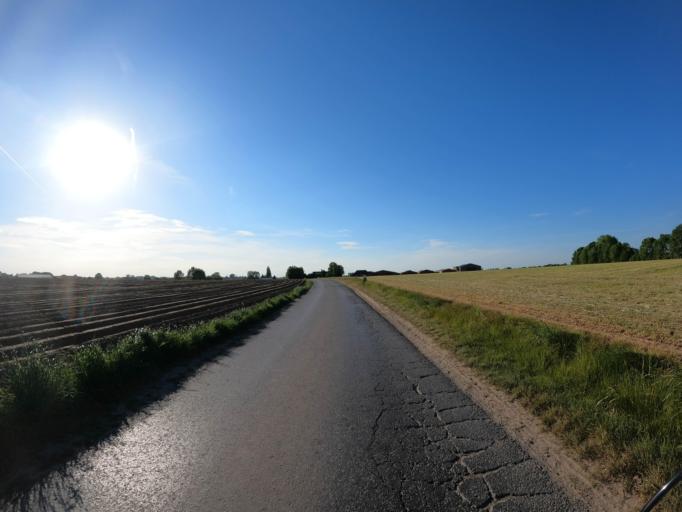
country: BE
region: Flanders
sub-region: Provincie West-Vlaanderen
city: Dentergem
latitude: 50.9901
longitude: 3.4595
